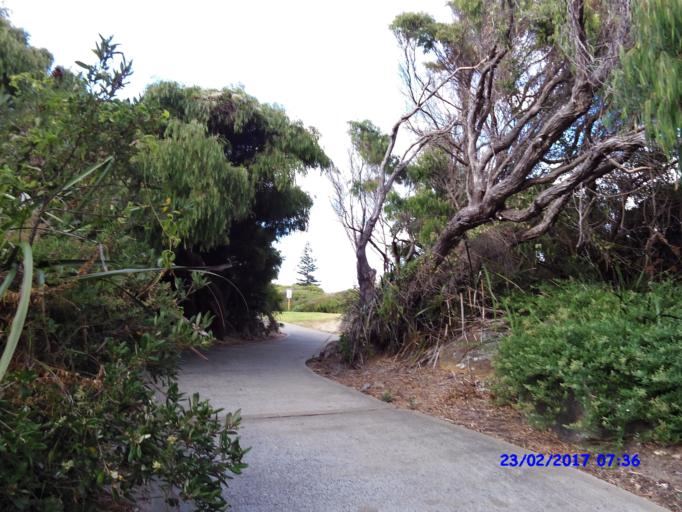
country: AU
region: Western Australia
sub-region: Augusta-Margaret River Shire
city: Augusta
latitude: -34.3258
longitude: 115.1702
